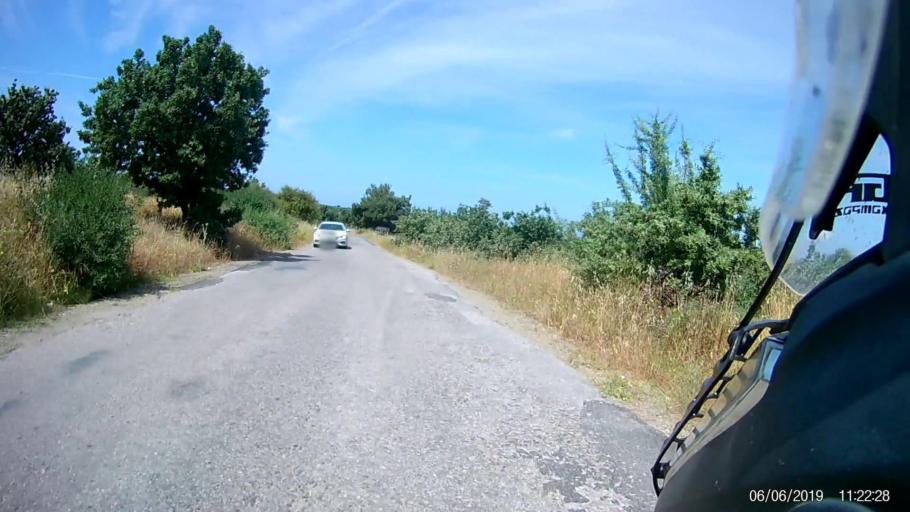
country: TR
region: Canakkale
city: Gulpinar
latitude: 39.6109
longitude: 26.1861
